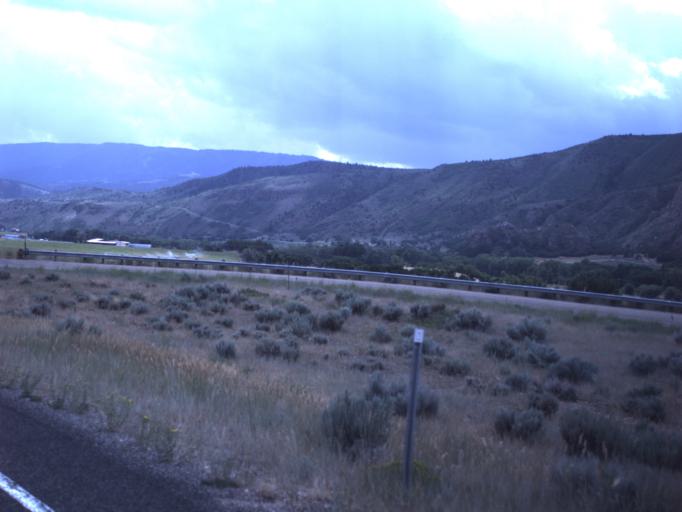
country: US
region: Utah
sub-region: Summit County
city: Francis
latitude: 40.4589
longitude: -110.8247
